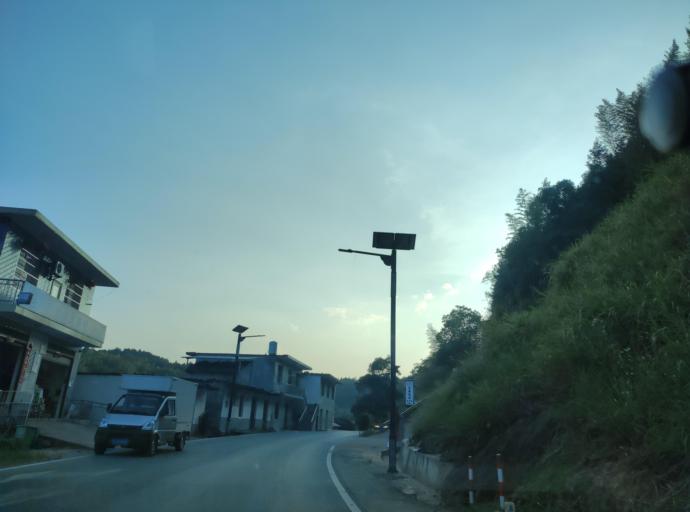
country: CN
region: Jiangxi Sheng
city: Zhangjiafang
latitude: 27.5284
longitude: 114.0308
